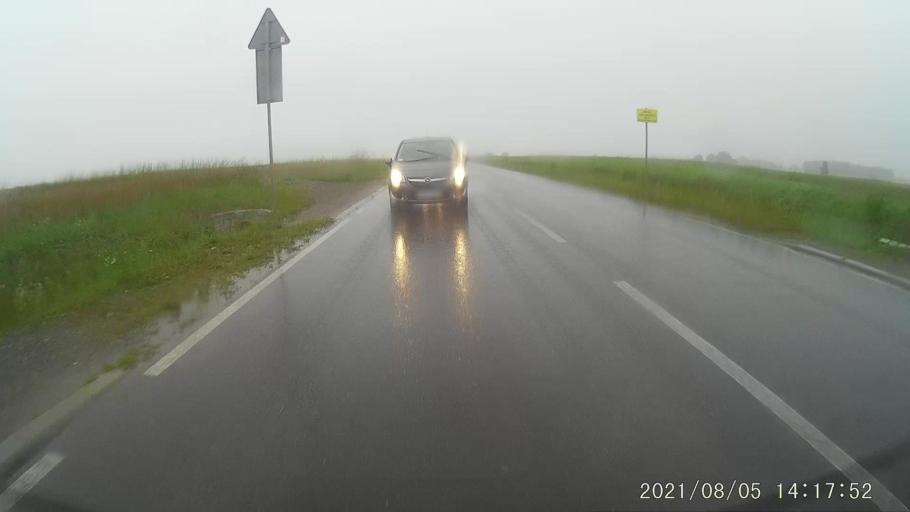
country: PL
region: Opole Voivodeship
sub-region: Powiat prudnicki
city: Biala
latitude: 50.4628
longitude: 17.7003
